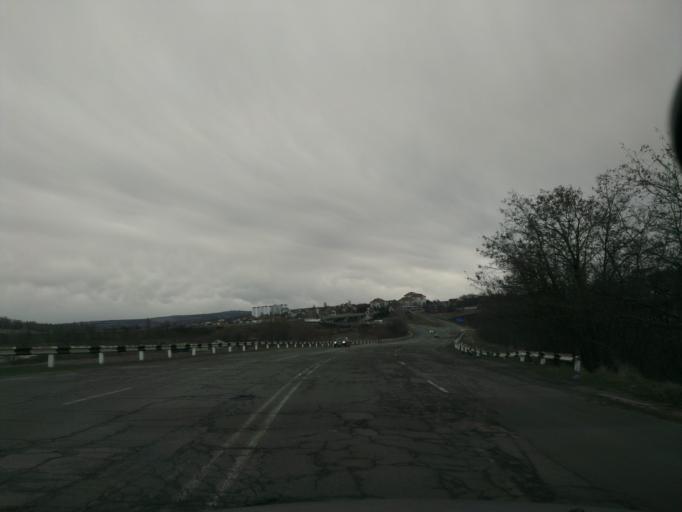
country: MD
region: Laloveni
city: Ialoveni
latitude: 46.9690
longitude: 28.7544
